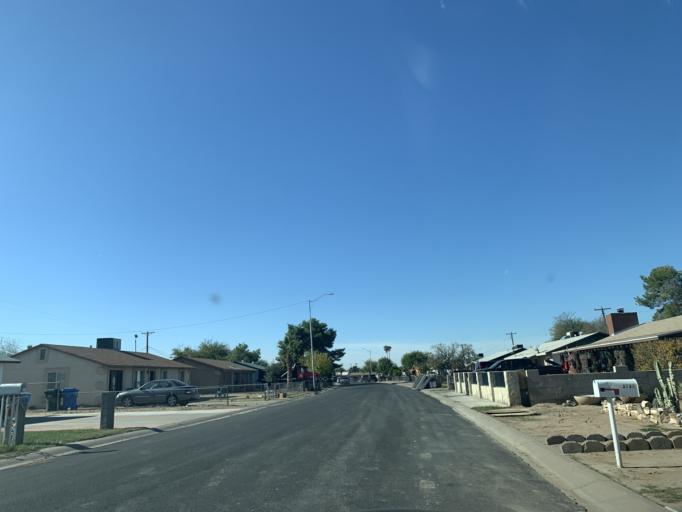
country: US
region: Arizona
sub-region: Maricopa County
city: Laveen
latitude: 33.3906
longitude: -112.1436
